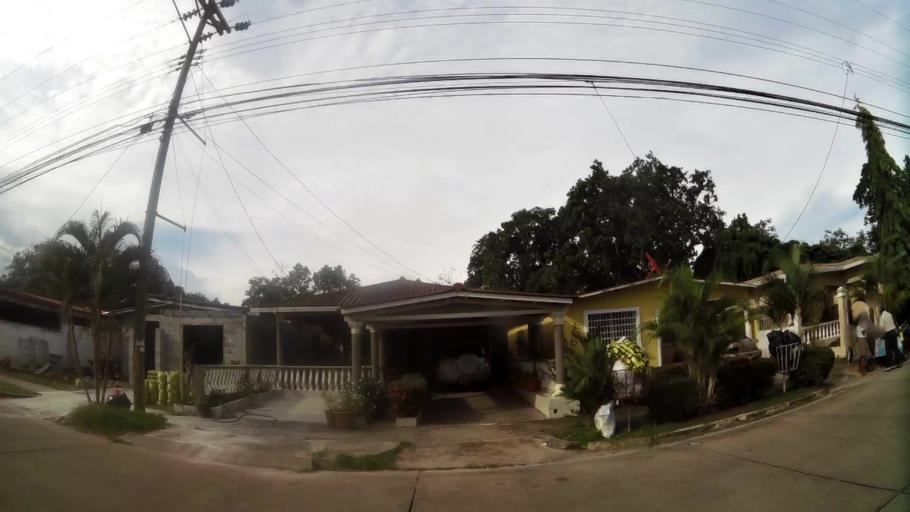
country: PA
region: Panama
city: La Chorrera
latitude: 8.8833
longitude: -79.7630
